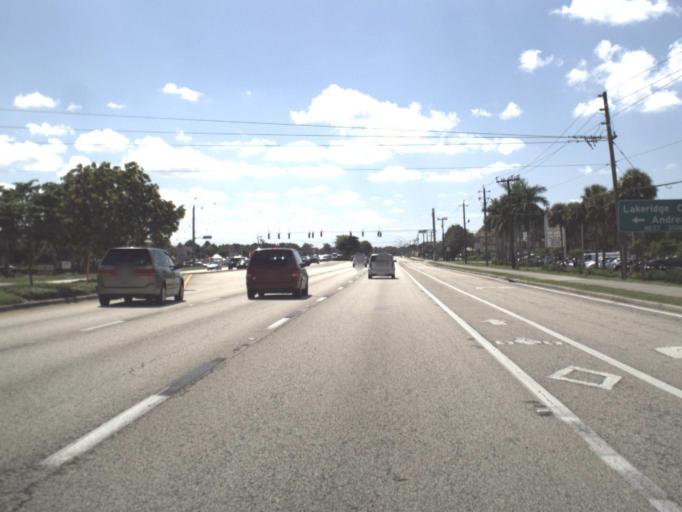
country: US
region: Florida
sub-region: Lee County
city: Villas
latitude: 26.5364
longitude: -81.8715
